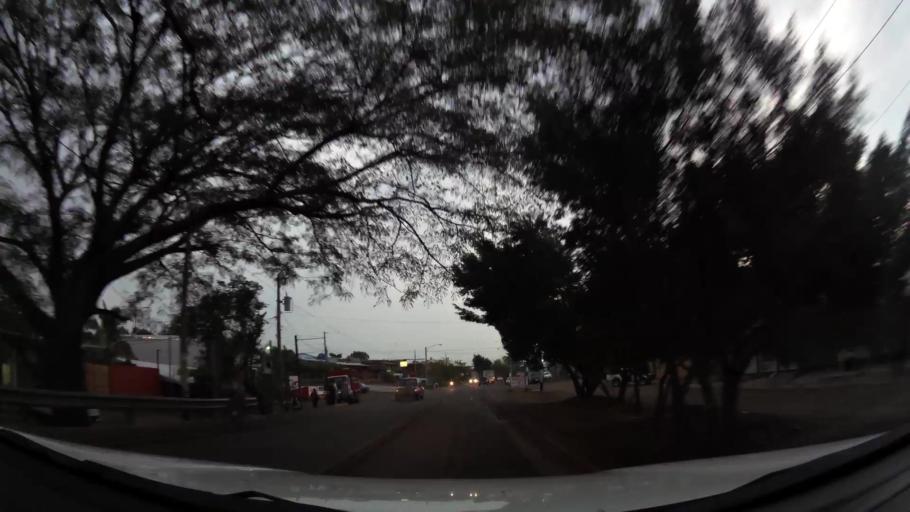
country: NI
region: Esteli
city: Esteli
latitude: 13.0738
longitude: -86.3525
